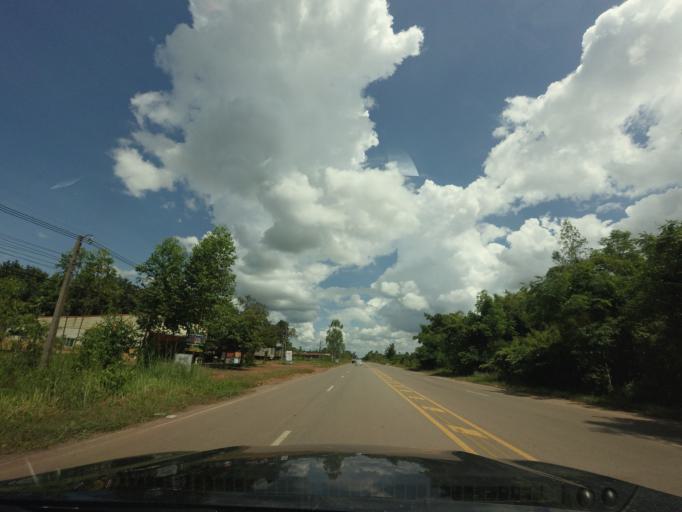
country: TH
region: Changwat Udon Thani
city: Ban Dung
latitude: 17.6821
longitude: 103.2228
